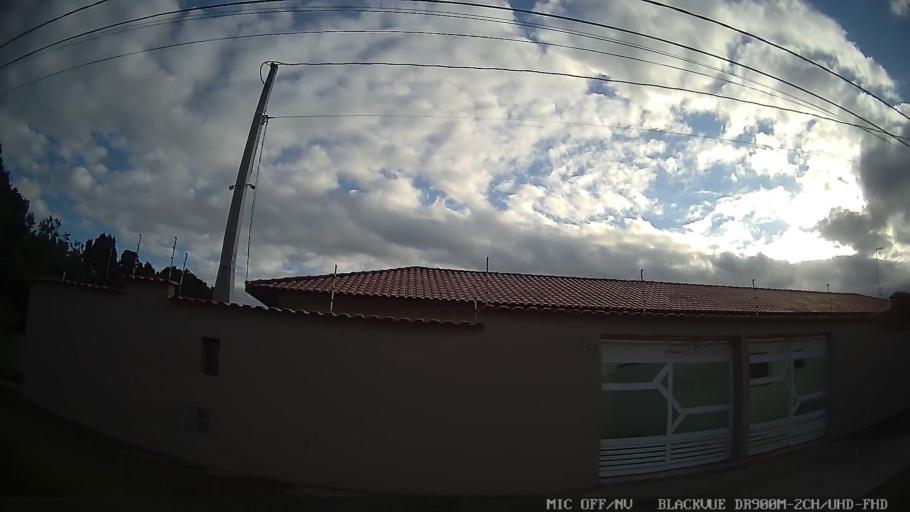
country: BR
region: Sao Paulo
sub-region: Itanhaem
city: Itanhaem
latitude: -24.1979
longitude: -46.8331
